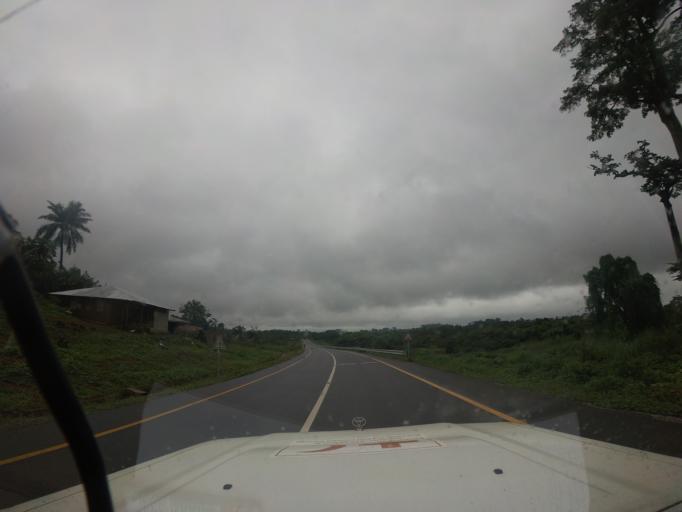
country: SL
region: Eastern Province
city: Hangha
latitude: 7.9415
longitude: -11.1396
